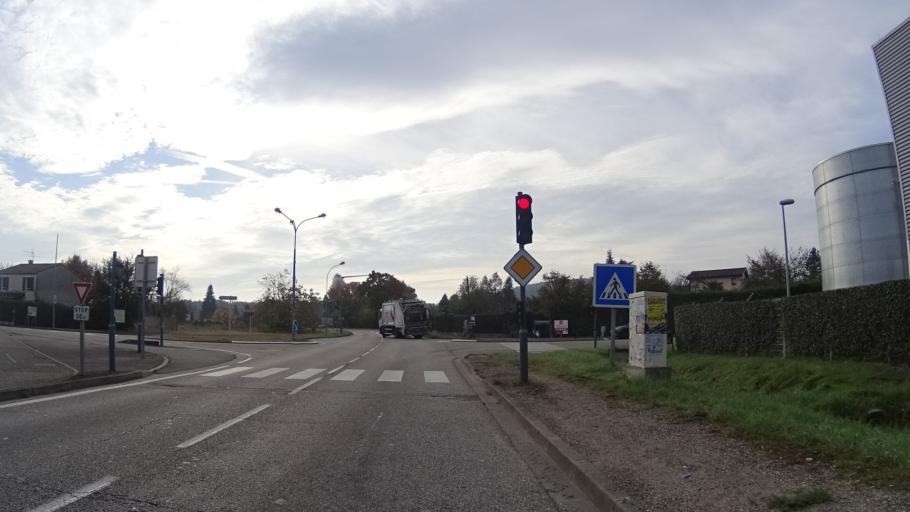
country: FR
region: Aquitaine
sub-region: Departement du Lot-et-Garonne
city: Boe
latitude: 44.1656
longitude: 0.6104
